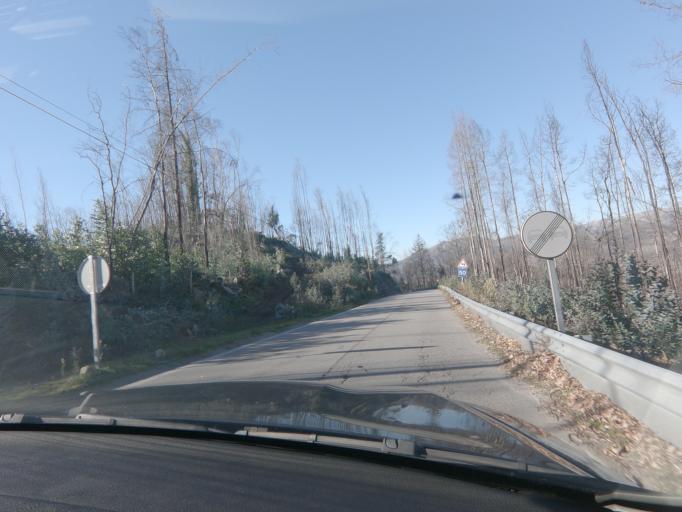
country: PT
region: Viseu
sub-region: Oliveira de Frades
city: Oliveira de Frades
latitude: 40.7313
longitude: -8.1483
